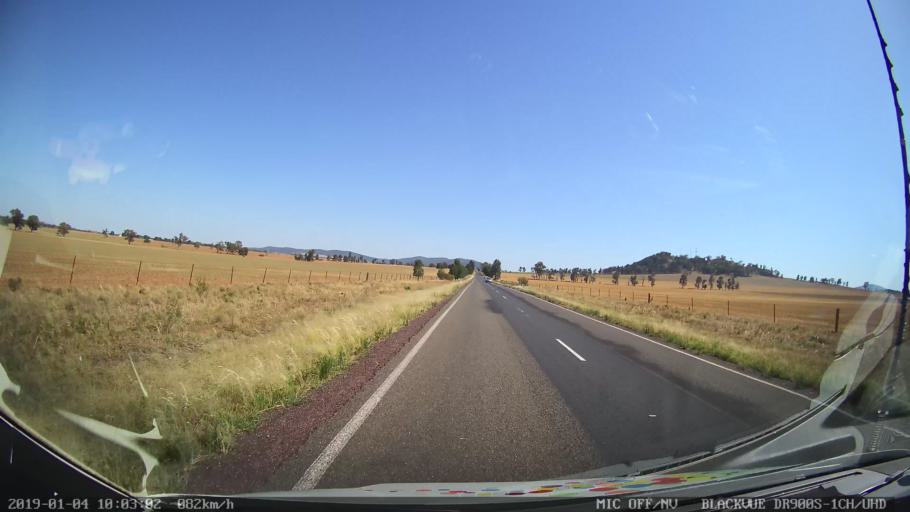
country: AU
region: New South Wales
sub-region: Cabonne
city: Canowindra
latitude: -33.4689
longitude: 148.3648
